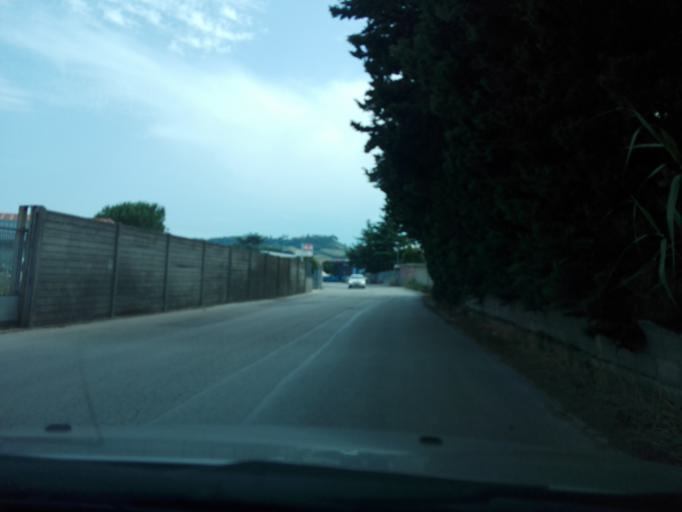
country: IT
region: Abruzzo
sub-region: Provincia di Pescara
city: Montesilvano Marina
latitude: 42.5075
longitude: 14.1306
